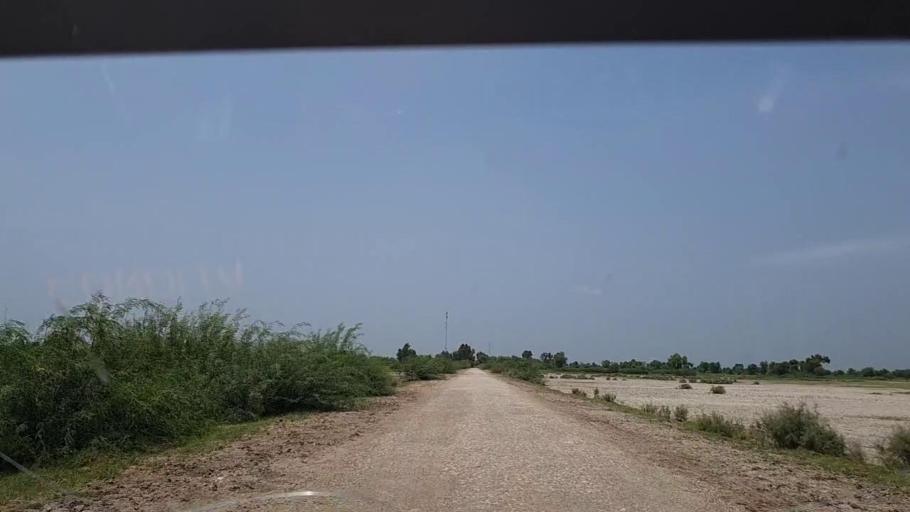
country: PK
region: Sindh
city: Adilpur
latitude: 27.9142
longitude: 69.2101
